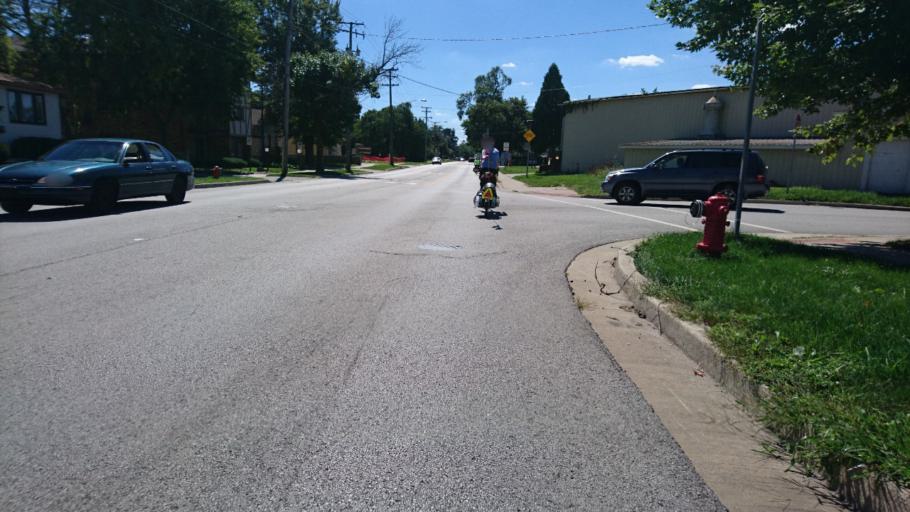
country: US
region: Illinois
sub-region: Cook County
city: Lansing
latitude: 41.5614
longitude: -87.5297
